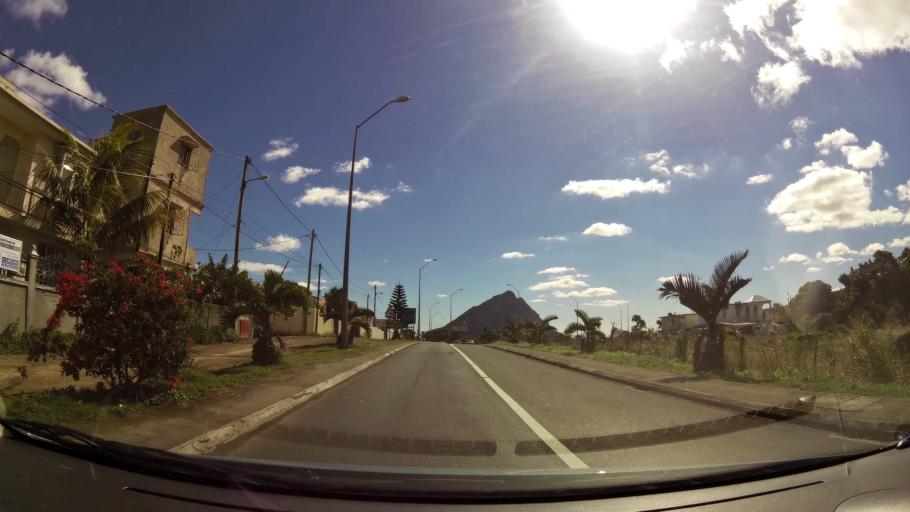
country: MU
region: Plaines Wilhems
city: Vacoas
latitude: -20.2877
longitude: 57.4775
